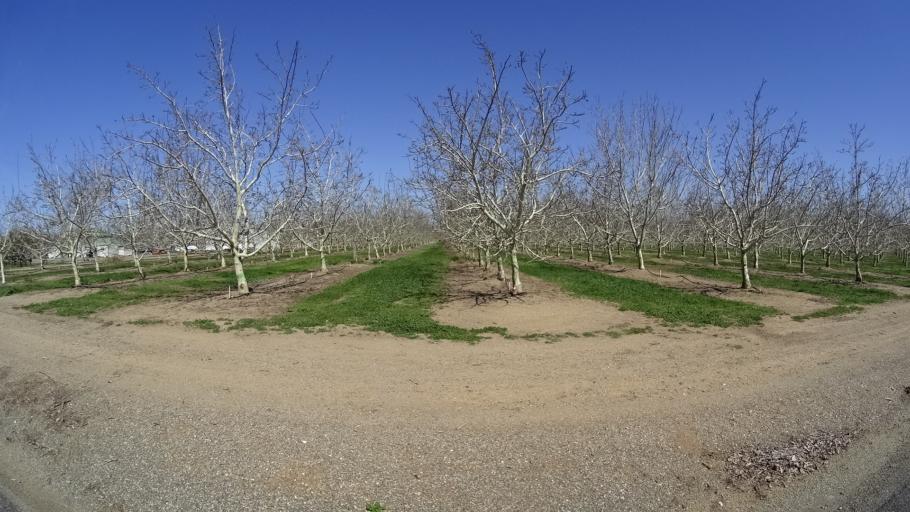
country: US
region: California
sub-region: Glenn County
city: Orland
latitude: 39.7897
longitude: -122.1176
